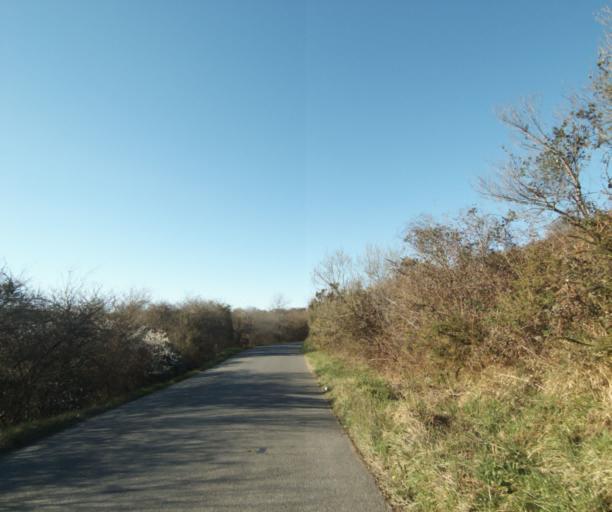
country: FR
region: Aquitaine
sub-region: Departement des Pyrenees-Atlantiques
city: Hendaye
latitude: 43.3565
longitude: -1.7511
